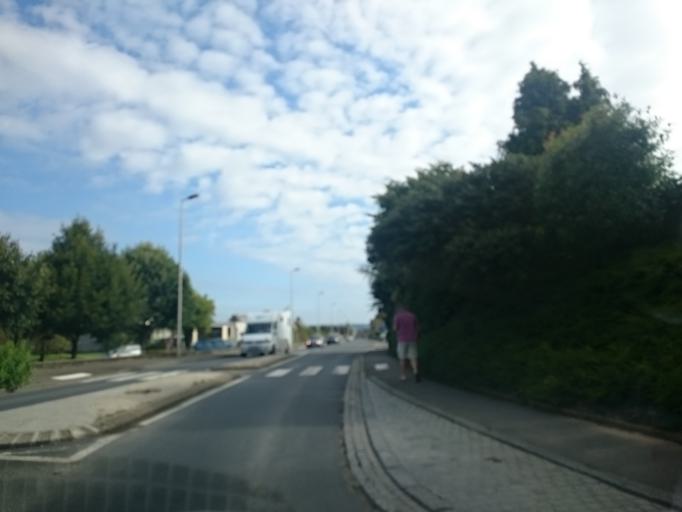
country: FR
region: Lower Normandy
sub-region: Departement de la Manche
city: Avranches
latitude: 48.6927
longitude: -1.3508
